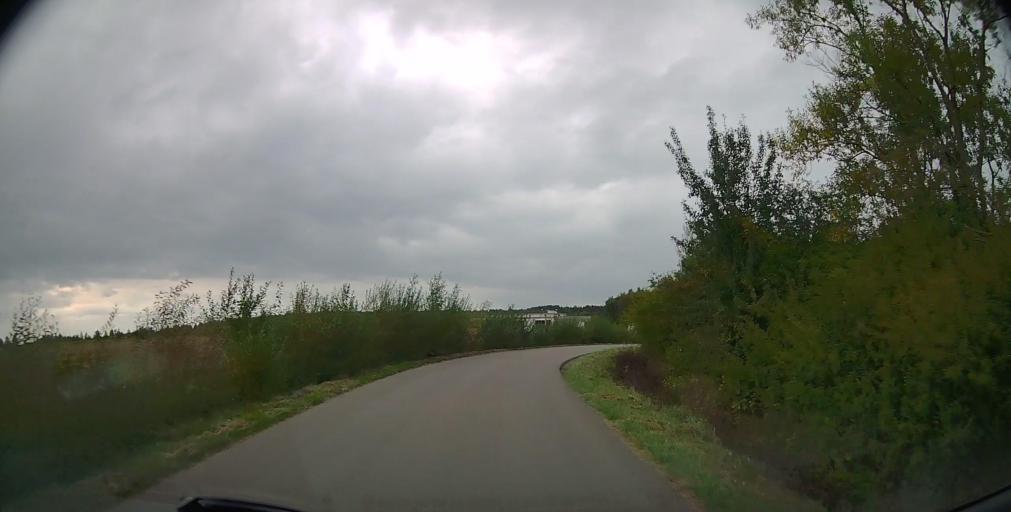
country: PL
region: Masovian Voivodeship
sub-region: Powiat radomski
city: Jedlinsk
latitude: 51.4538
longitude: 21.1034
